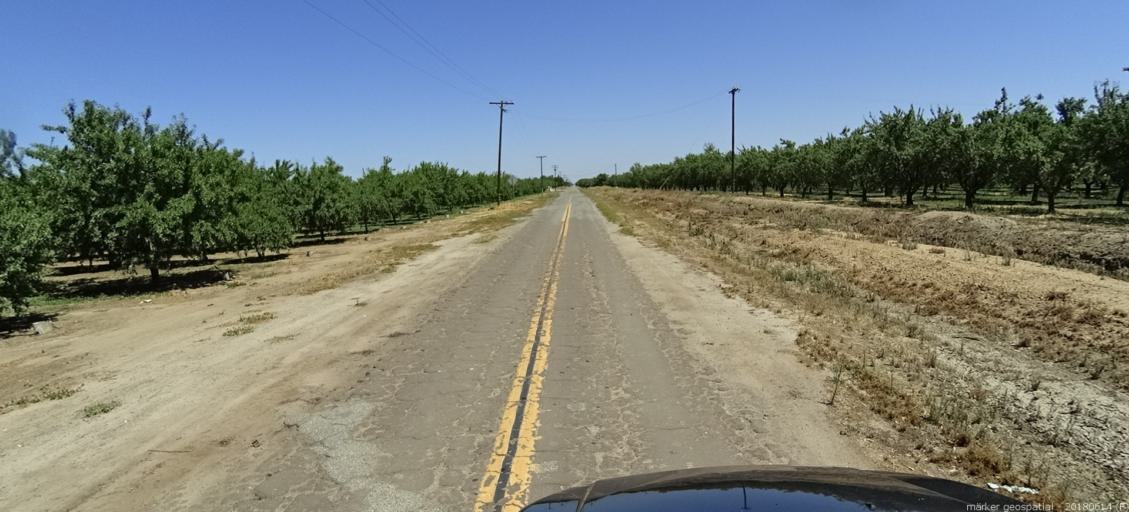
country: US
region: California
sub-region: Madera County
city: Fairmead
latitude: 37.0052
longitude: -120.2386
